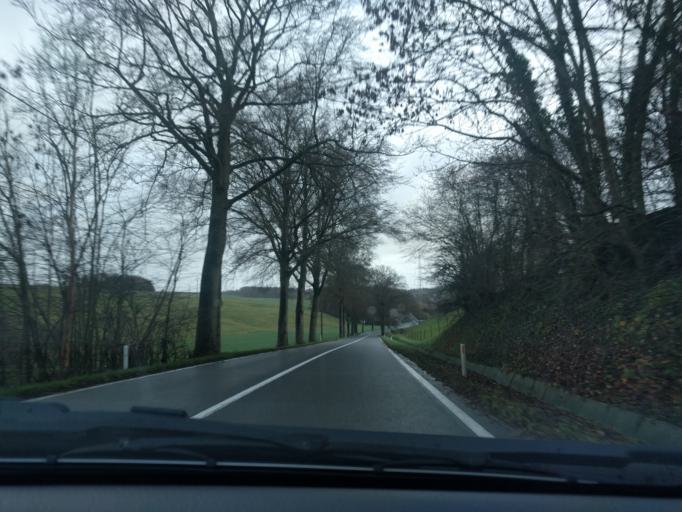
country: BE
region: Wallonia
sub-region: Province de Namur
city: Noville-les-Bois
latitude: 50.5037
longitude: 4.9448
